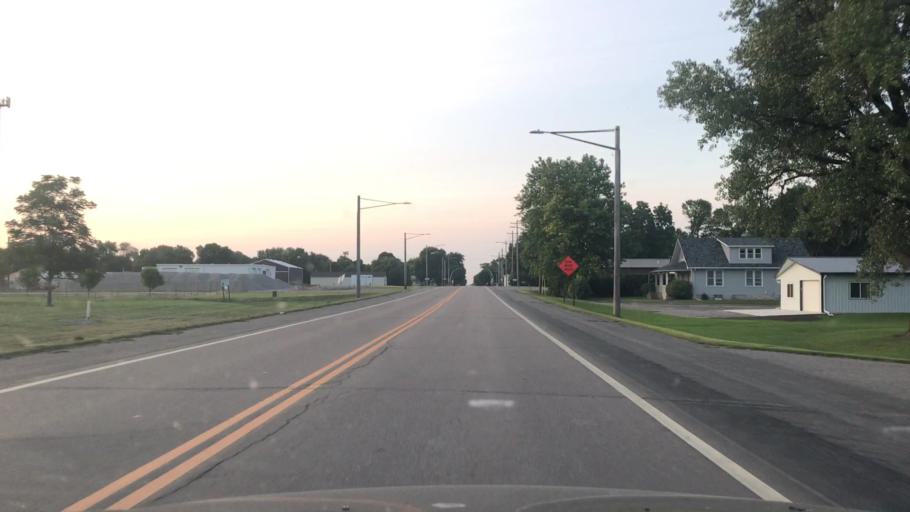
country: US
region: Minnesota
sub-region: Redwood County
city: Redwood Falls
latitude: 44.5294
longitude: -95.1195
